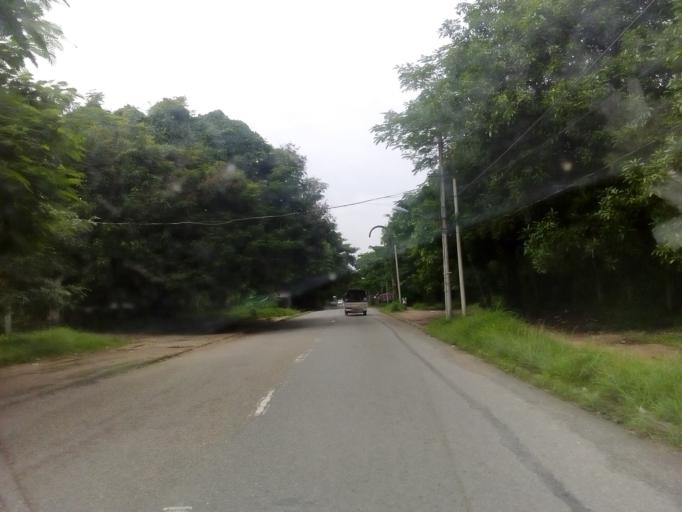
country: MM
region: Yangon
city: Yangon
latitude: 16.8539
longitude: 96.1299
